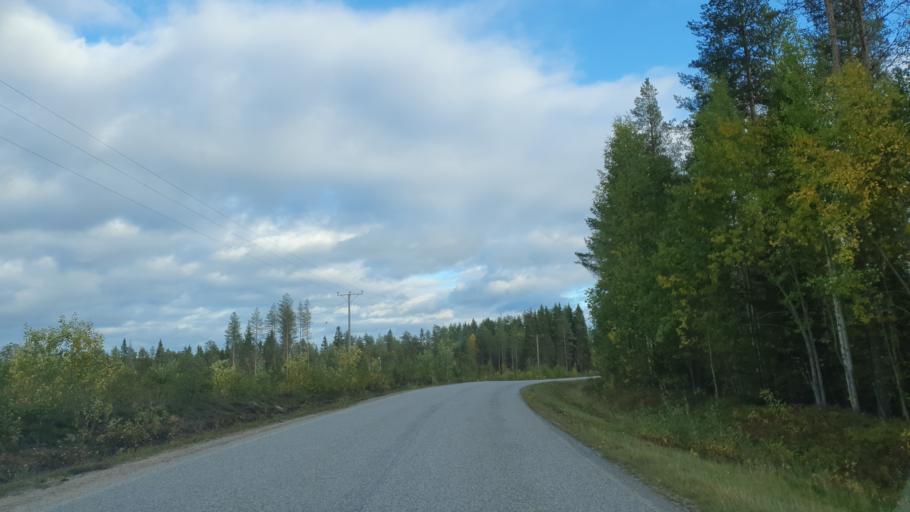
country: FI
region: Kainuu
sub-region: Kehys-Kainuu
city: Kuhmo
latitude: 63.9311
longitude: 29.9921
